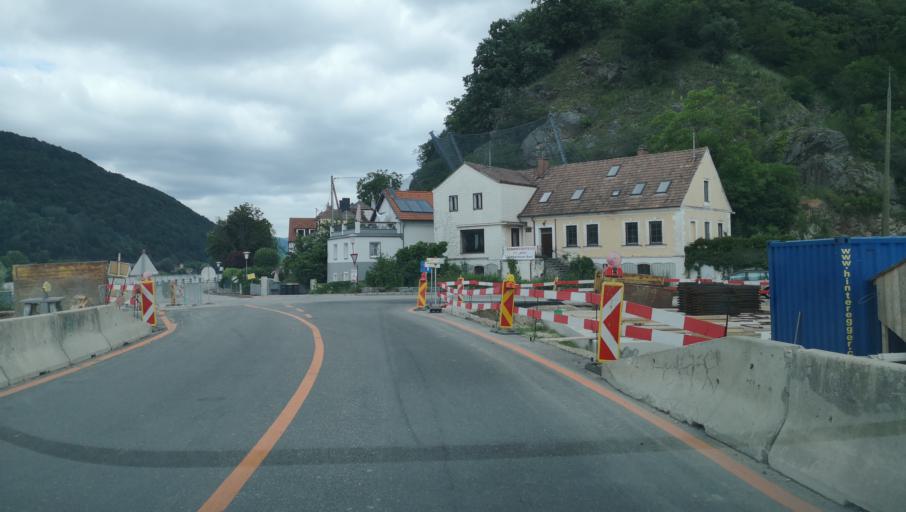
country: AT
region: Lower Austria
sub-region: Politischer Bezirk Krems
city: Aggsbach
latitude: 48.2922
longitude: 15.4077
